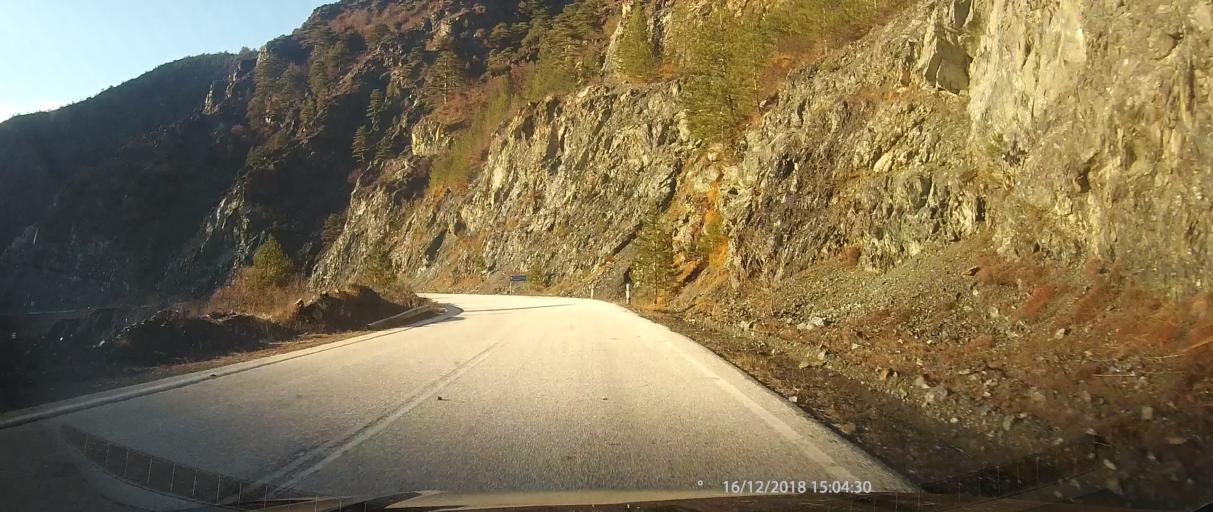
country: GR
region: West Macedonia
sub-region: Nomos Kastorias
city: Nestorio
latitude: 40.2280
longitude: 20.9681
